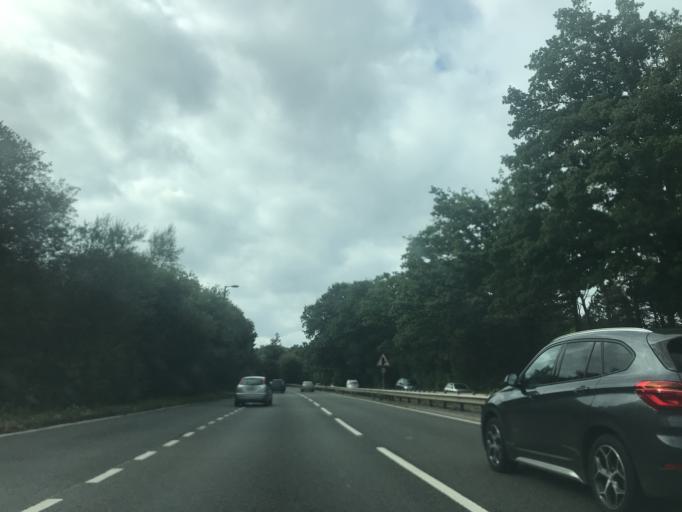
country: GB
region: England
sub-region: Surrey
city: Bagshot
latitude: 51.3709
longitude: -0.6883
